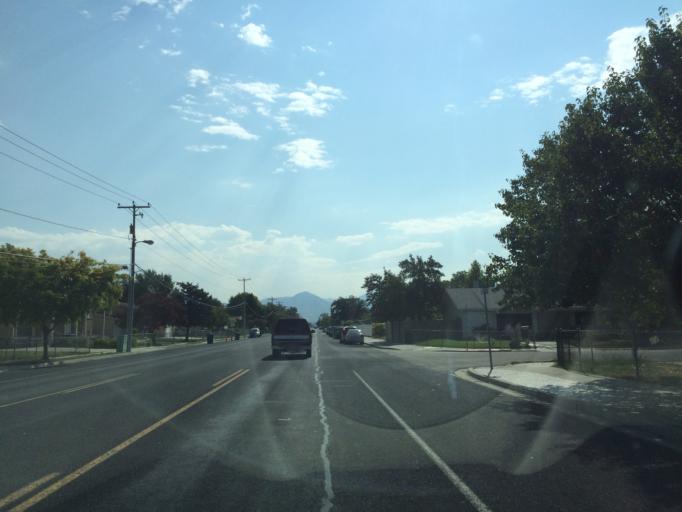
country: US
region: Utah
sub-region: Salt Lake County
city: West Valley City
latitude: 40.7039
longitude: -111.9944
